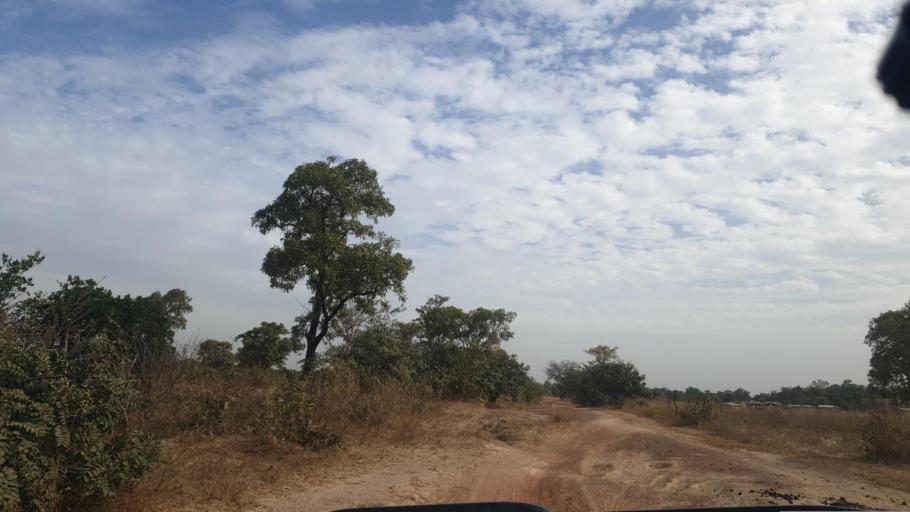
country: ML
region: Sikasso
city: Yanfolila
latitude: 11.4110
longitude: -8.0065
